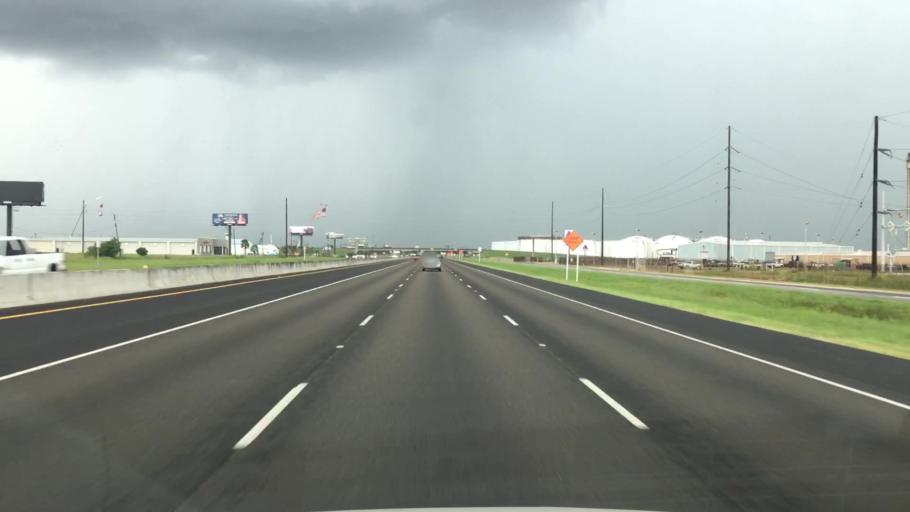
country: US
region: Texas
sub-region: Nueces County
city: Corpus Christi
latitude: 27.8084
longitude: -97.4960
